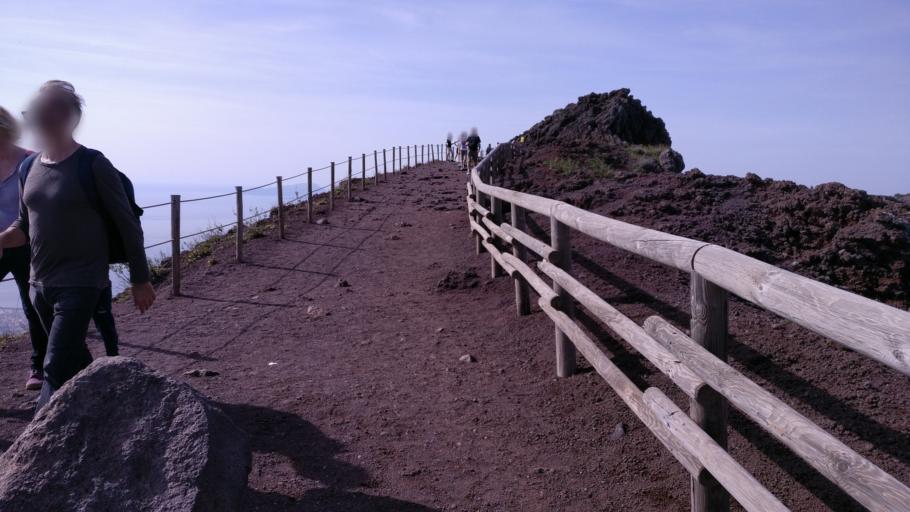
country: IT
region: Campania
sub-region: Provincia di Napoli
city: Torre del Greco
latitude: 40.8188
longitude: 14.4265
